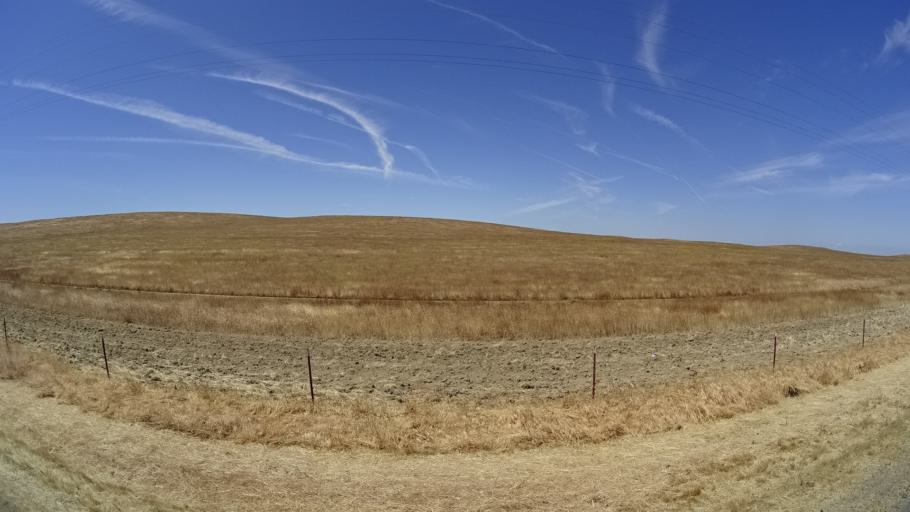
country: US
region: California
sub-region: Kings County
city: Kettleman City
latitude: 35.8724
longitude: -119.9153
